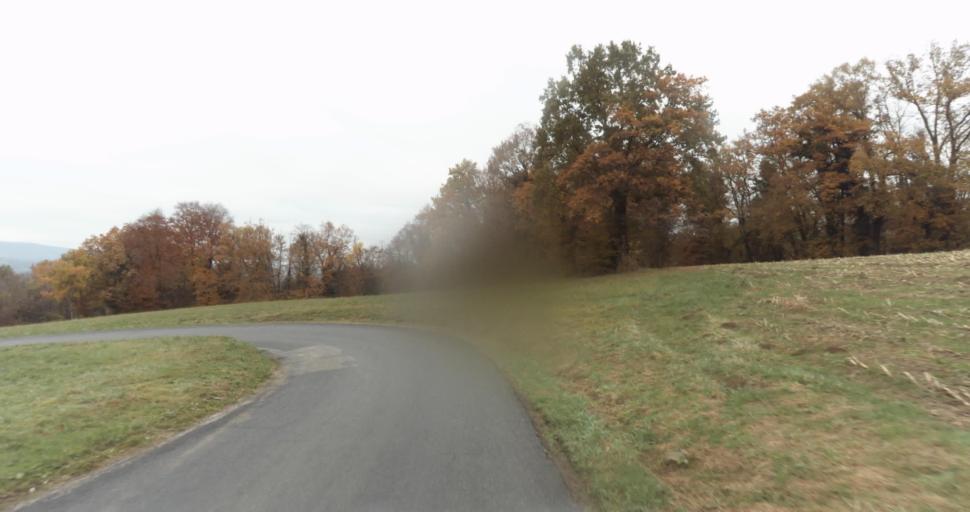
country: FR
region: Rhone-Alpes
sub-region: Departement de la Savoie
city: Albens
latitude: 45.7593
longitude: 5.9703
